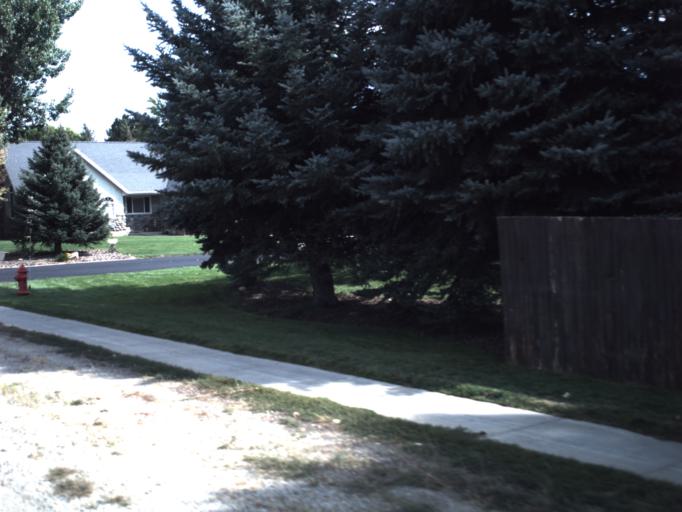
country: US
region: Utah
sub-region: Wasatch County
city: Midway
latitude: 40.5044
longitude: -111.4724
